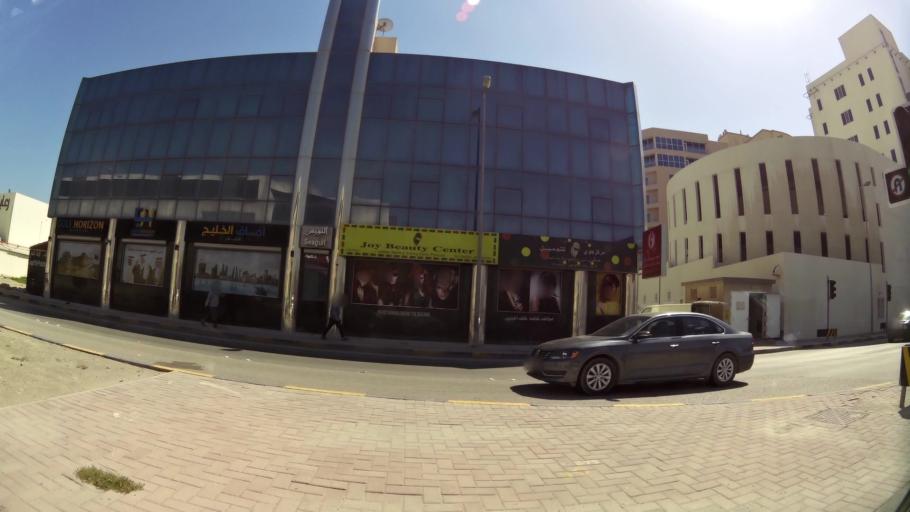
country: BH
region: Manama
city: Manama
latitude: 26.2126
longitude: 50.5778
